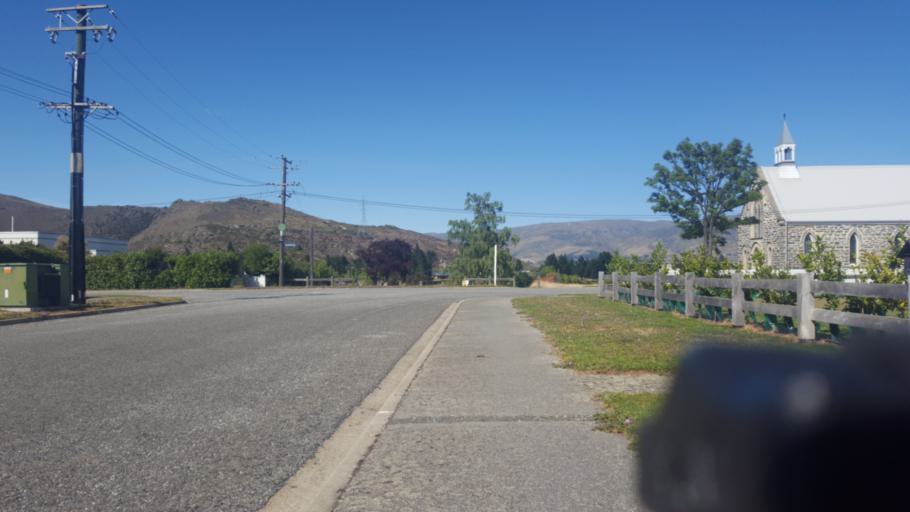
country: NZ
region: Otago
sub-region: Queenstown-Lakes District
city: Wanaka
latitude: -45.0489
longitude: 169.2104
